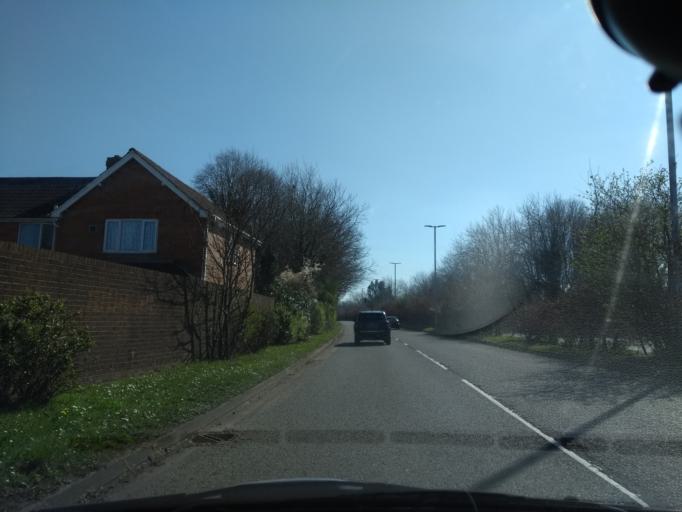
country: GB
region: England
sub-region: Somerset
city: Taunton
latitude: 51.0202
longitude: -3.0903
